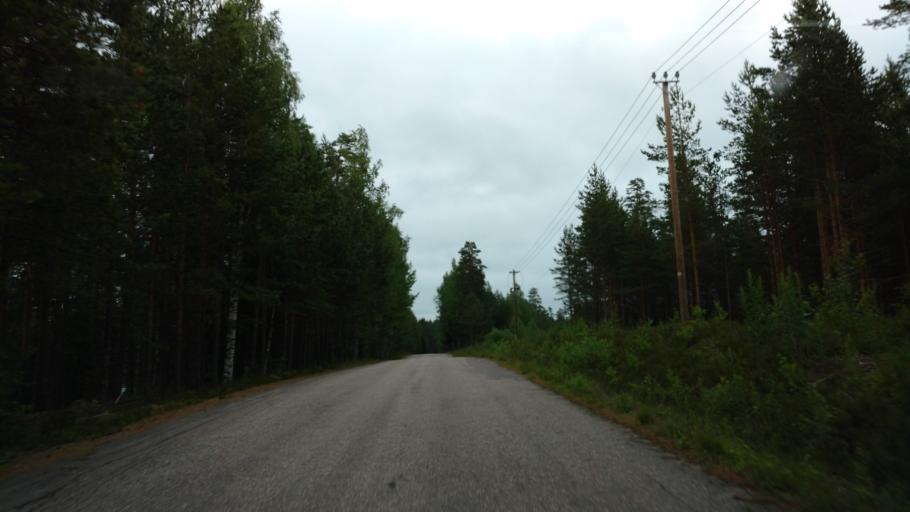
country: FI
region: Varsinais-Suomi
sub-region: Salo
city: Kiikala
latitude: 60.4714
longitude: 23.6523
